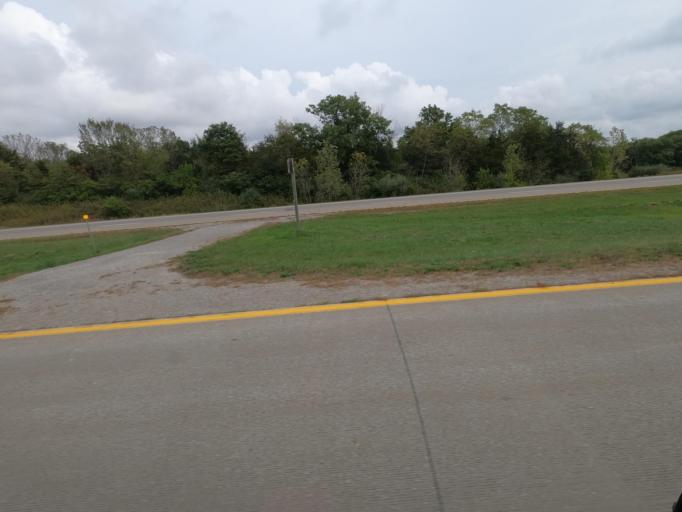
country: US
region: Iowa
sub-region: Wapello County
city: Ottumwa
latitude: 41.0407
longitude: -92.3724
